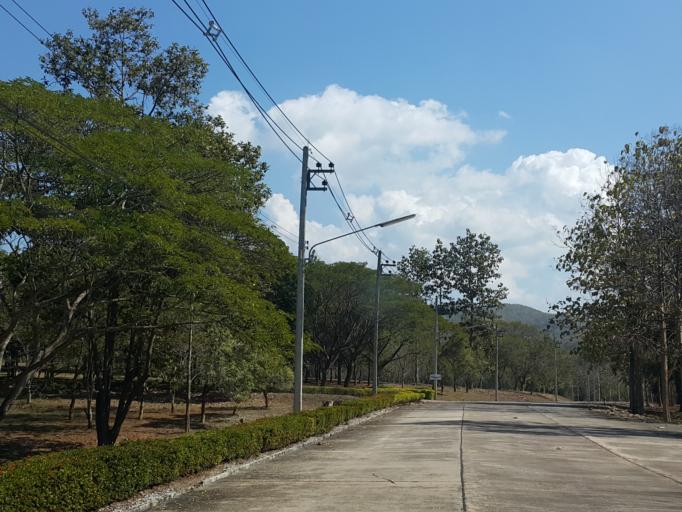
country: TH
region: Chiang Mai
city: Mae Taeng
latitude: 19.0221
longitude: 98.9899
